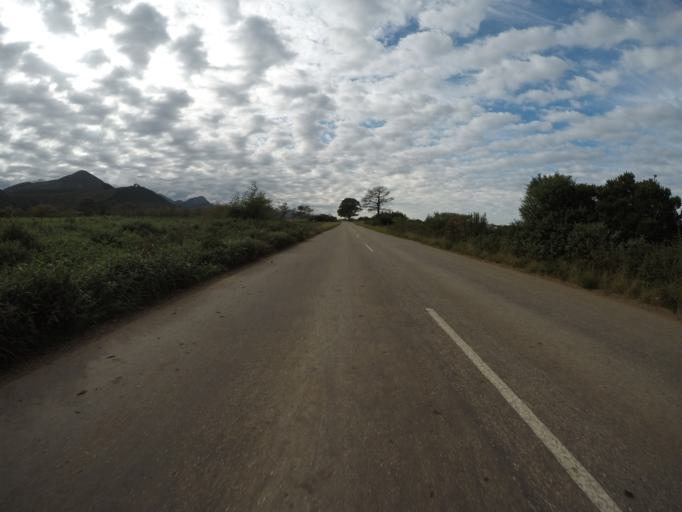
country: ZA
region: Eastern Cape
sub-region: Cacadu District Municipality
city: Kareedouw
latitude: -34.0096
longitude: 24.2730
